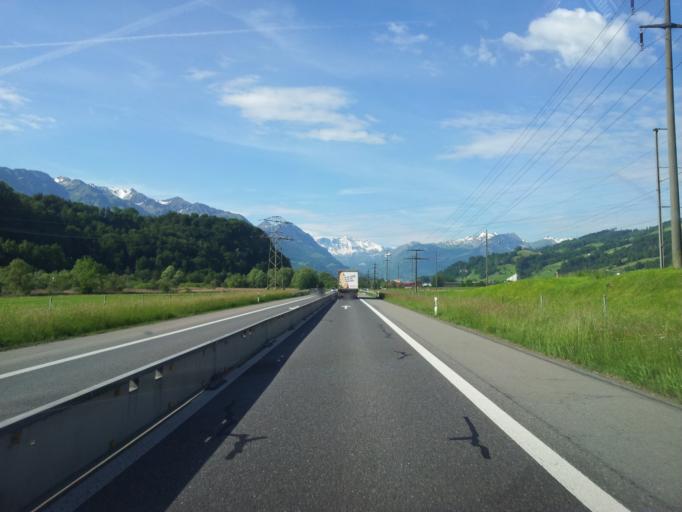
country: CH
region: Obwalden
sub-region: Obwalden
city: Kerns
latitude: 46.9213
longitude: 8.2715
